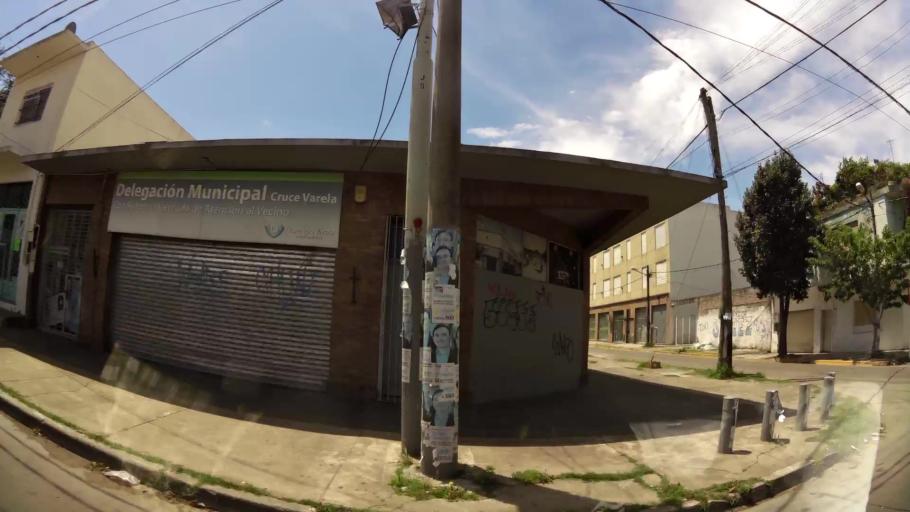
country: AR
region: Buenos Aires
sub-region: Partido de Quilmes
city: Quilmes
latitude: -34.7819
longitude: -58.2627
